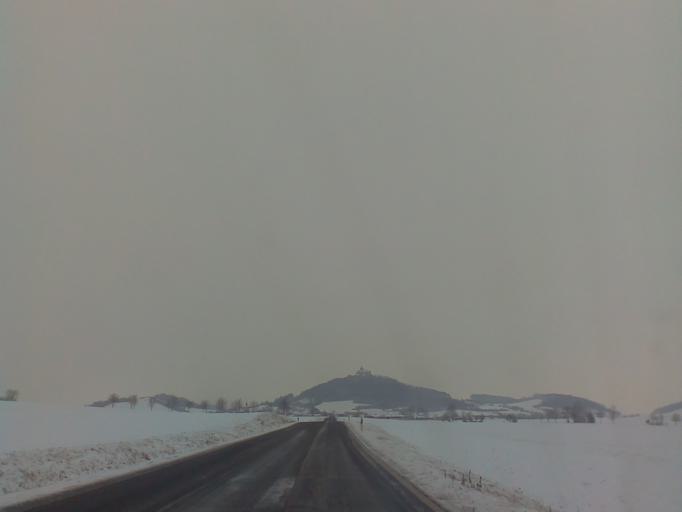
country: DE
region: Thuringia
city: Arnstadt
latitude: 50.8462
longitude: 10.9021
